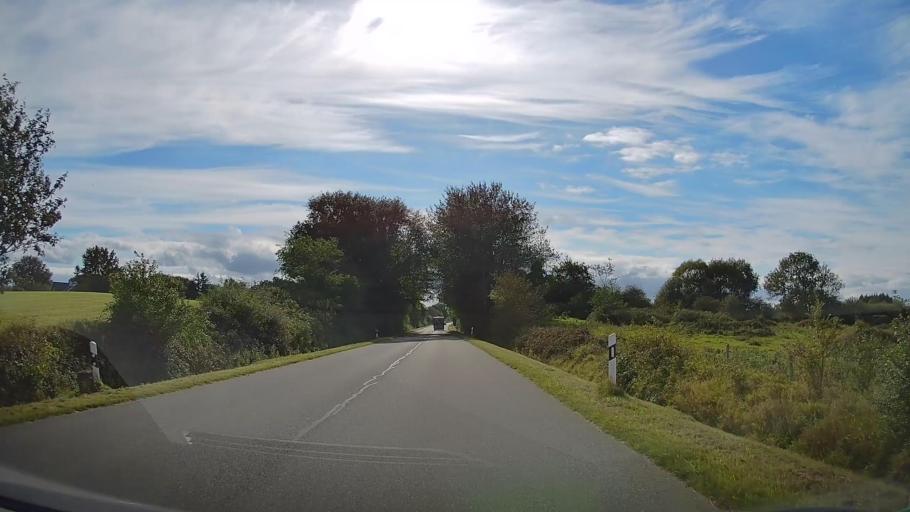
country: DK
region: South Denmark
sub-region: Sonderborg Kommune
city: Grasten
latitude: 54.8683
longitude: 9.5956
